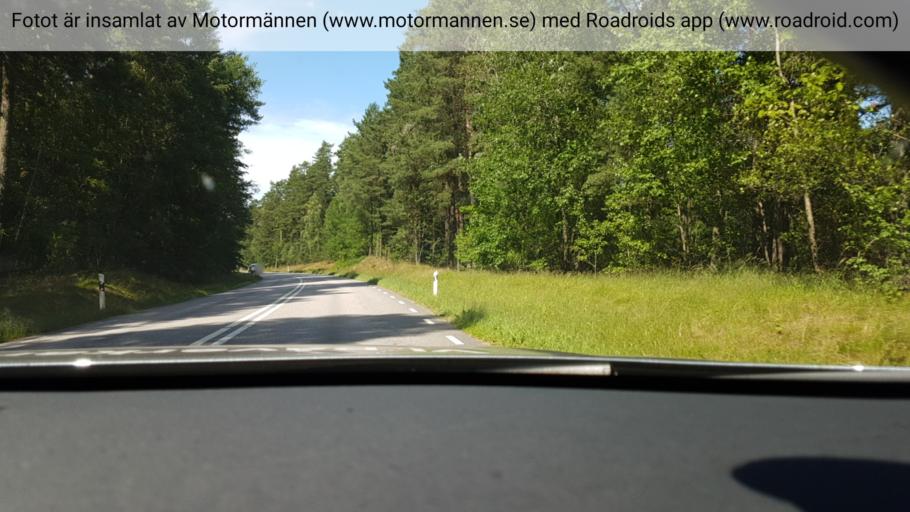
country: SE
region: Vaestra Goetaland
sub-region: Skovde Kommun
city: Stopen
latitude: 58.4673
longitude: 13.9585
